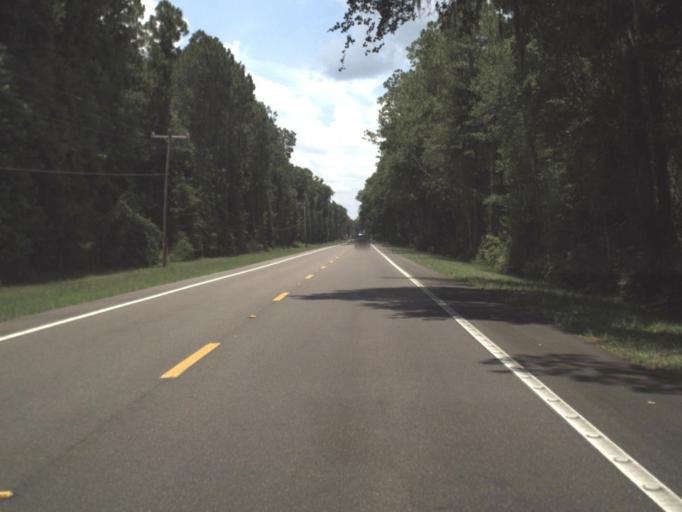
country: US
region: Florida
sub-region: Alachua County
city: Gainesville
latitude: 29.6811
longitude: -82.2323
